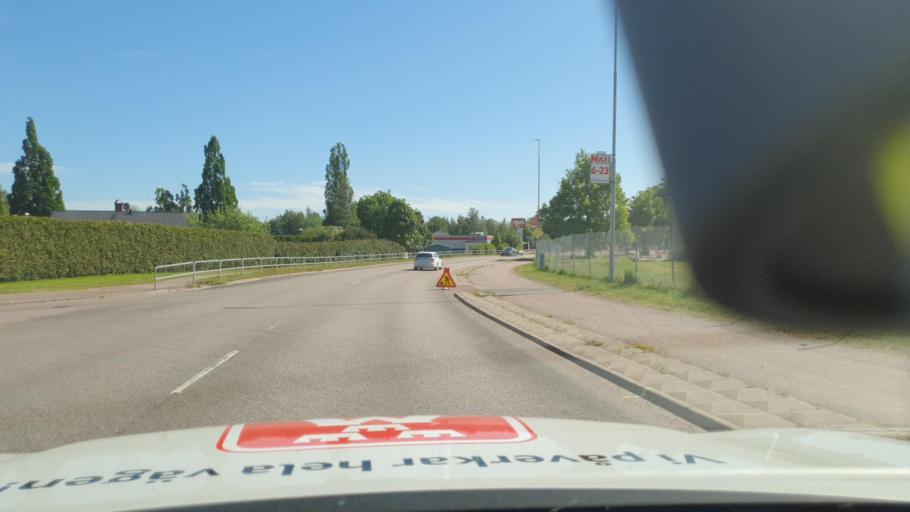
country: SE
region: Vaermland
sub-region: Kristinehamns Kommun
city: Kristinehamn
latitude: 59.3216
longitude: 14.1139
